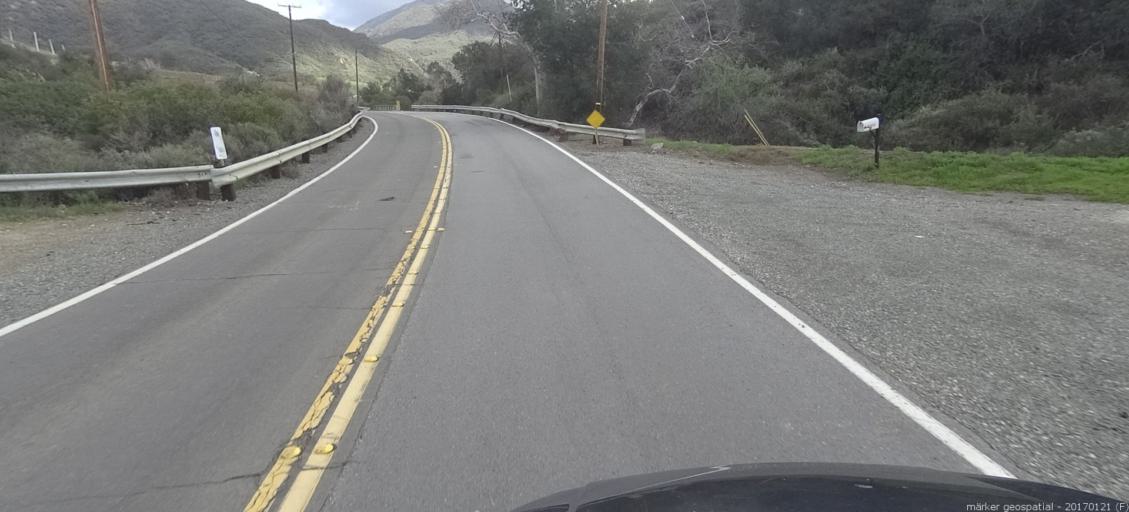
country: US
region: California
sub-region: Orange County
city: Foothill Ranch
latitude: 33.7453
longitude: -117.6512
